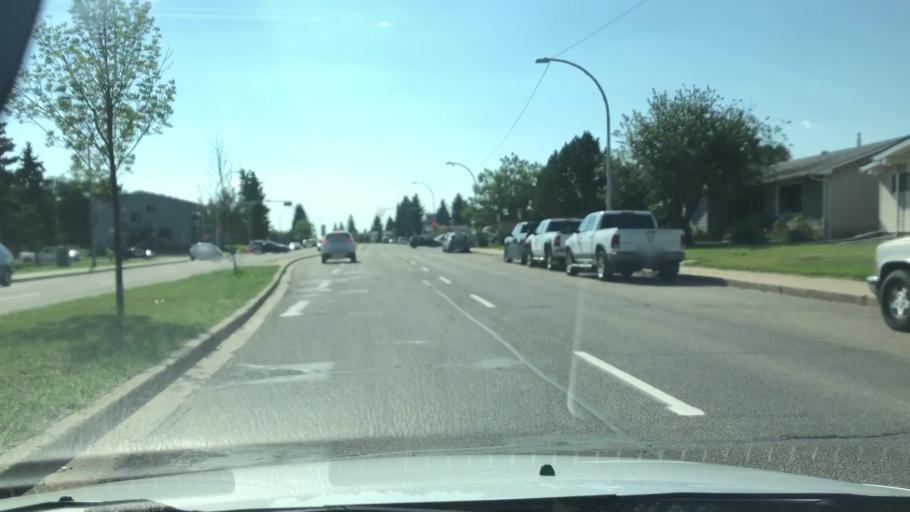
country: CA
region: Alberta
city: Edmonton
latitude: 53.6070
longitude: -113.4658
